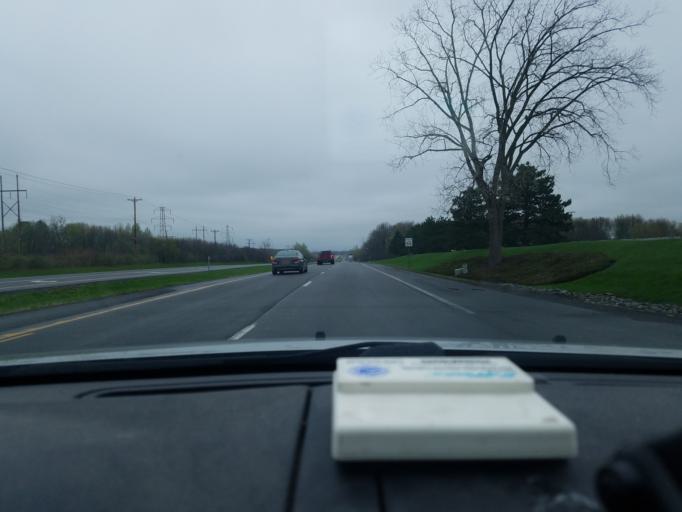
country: US
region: New York
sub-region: Onondaga County
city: East Syracuse
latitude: 43.1062
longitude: -76.0769
